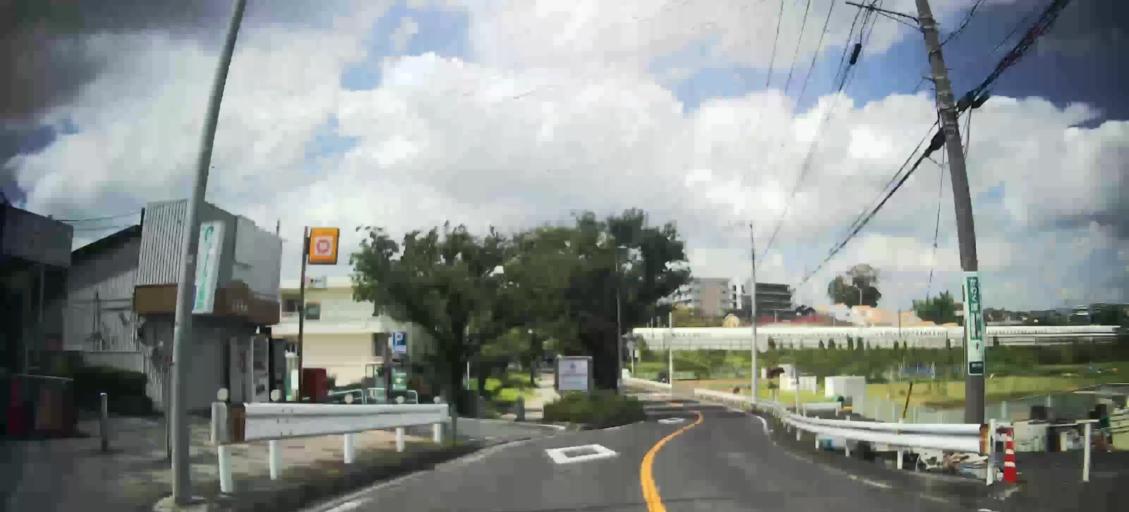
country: JP
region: Kanagawa
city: Yokohama
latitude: 35.4709
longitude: 139.5549
